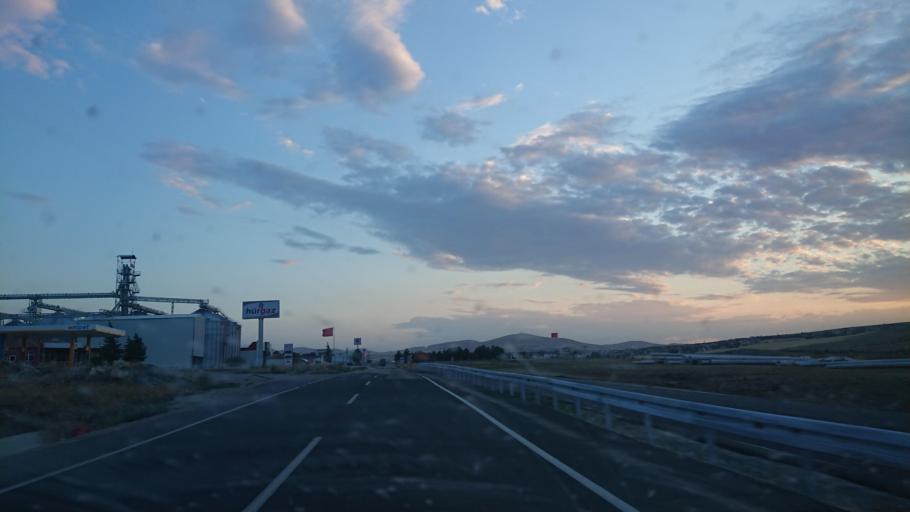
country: TR
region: Aksaray
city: Balci
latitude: 38.7664
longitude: 34.0948
